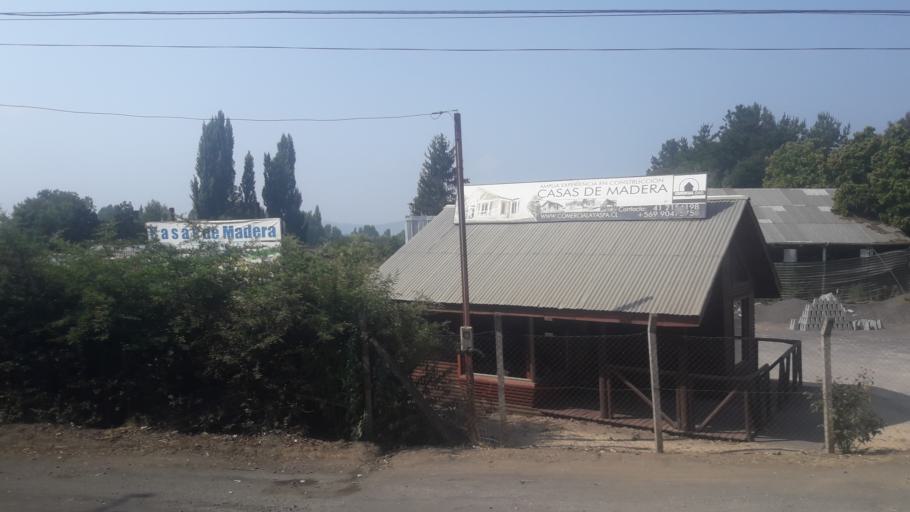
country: CL
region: Biobio
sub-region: Provincia de Concepcion
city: Lota
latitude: -37.1627
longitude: -72.9585
